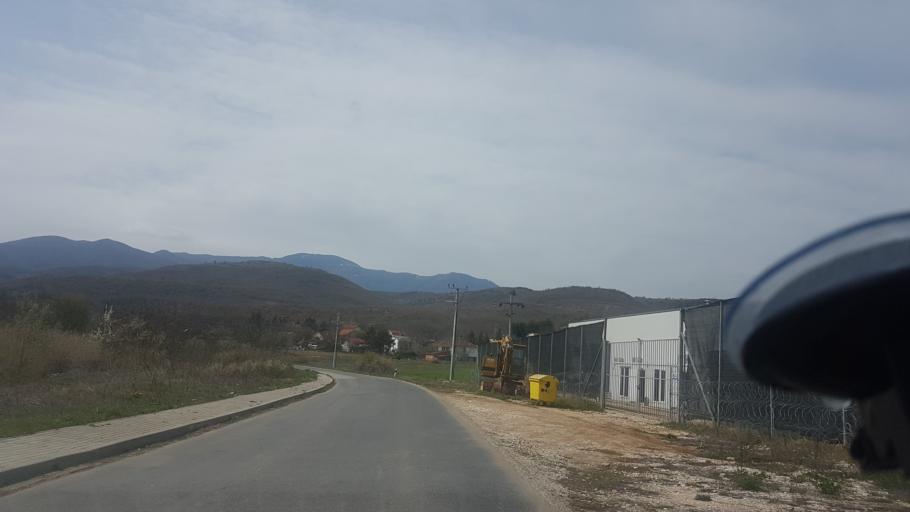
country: MK
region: Zelenikovo
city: Zelenikovo
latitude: 41.8928
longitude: 21.5906
